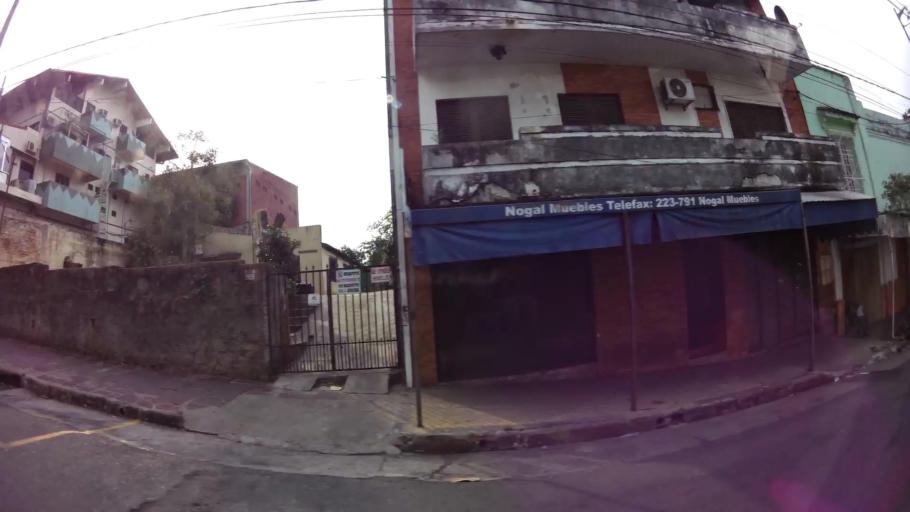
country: PY
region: Asuncion
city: Asuncion
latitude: -25.2969
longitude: -57.6265
